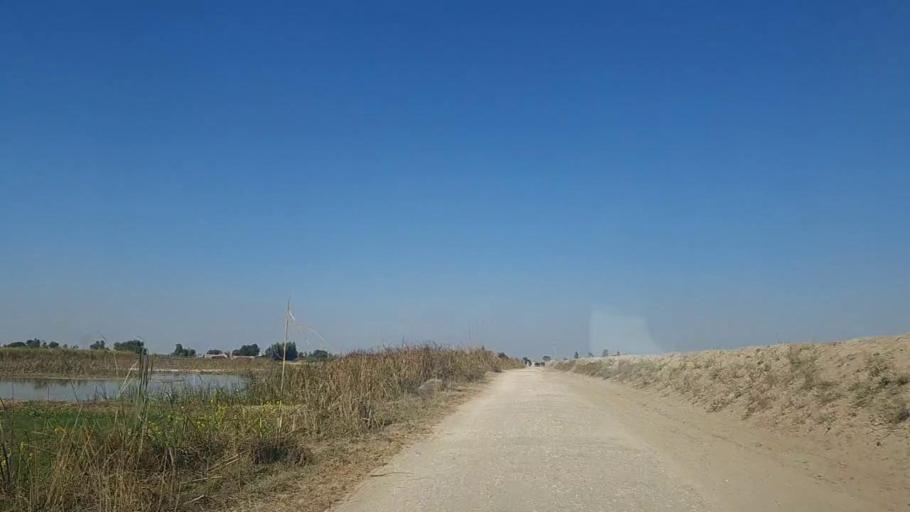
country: PK
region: Sindh
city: Sanghar
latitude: 26.2161
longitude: 68.9292
